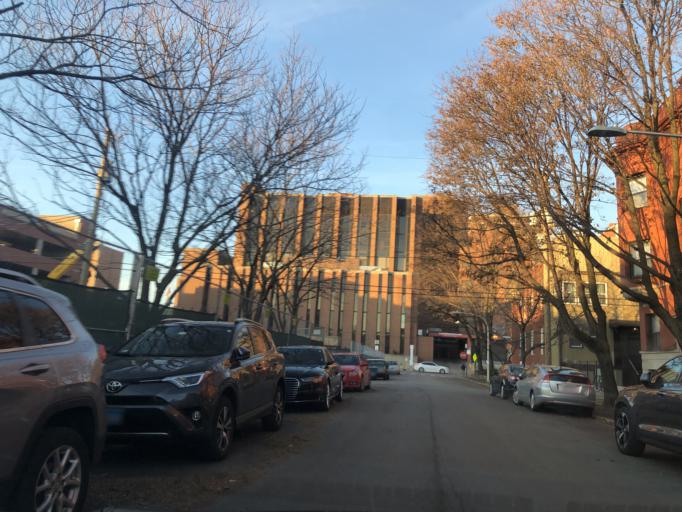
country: US
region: Illinois
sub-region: Cook County
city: Chicago
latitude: 41.9355
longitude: -87.6516
